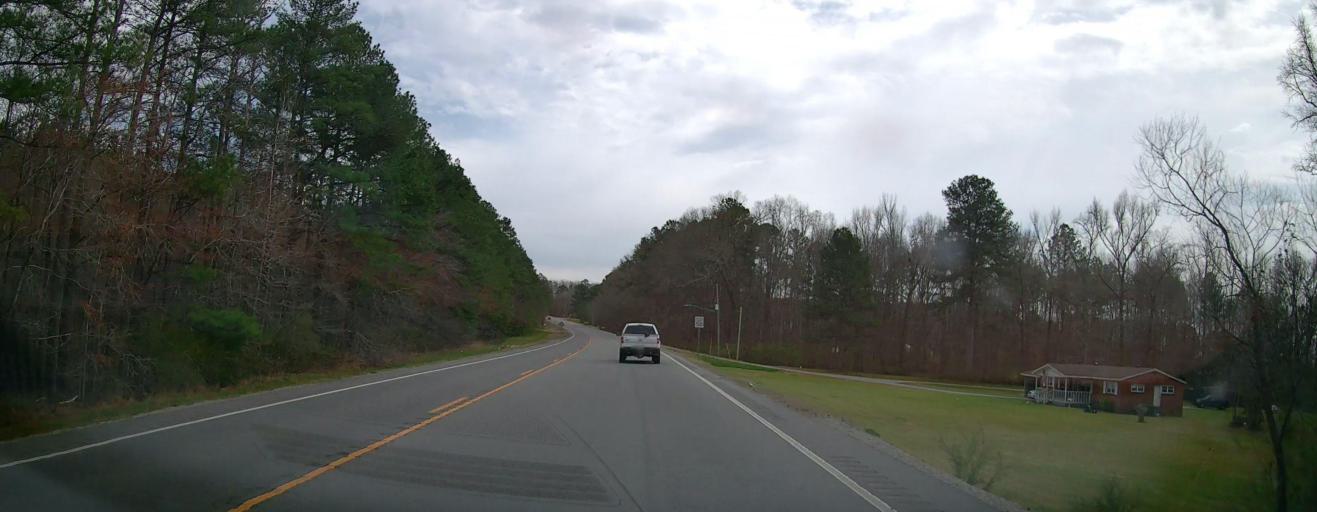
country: US
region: Alabama
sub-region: Marion County
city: Guin
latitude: 33.9936
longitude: -87.9283
